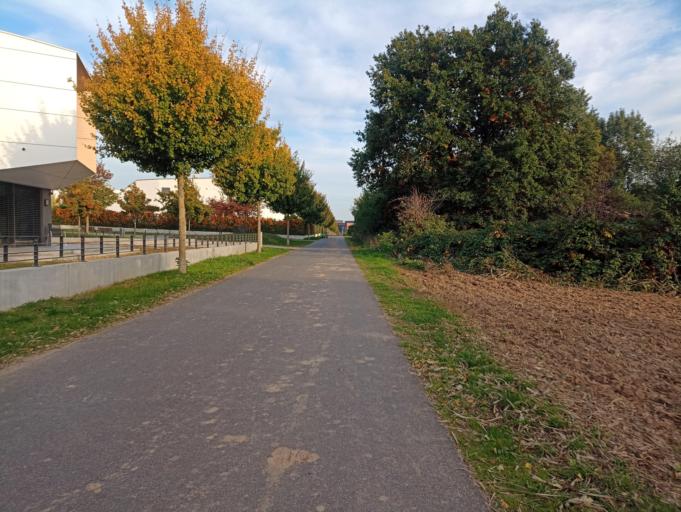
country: DE
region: Hesse
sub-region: Regierungsbezirk Darmstadt
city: Steinbach am Taunus
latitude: 50.1742
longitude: 8.6192
